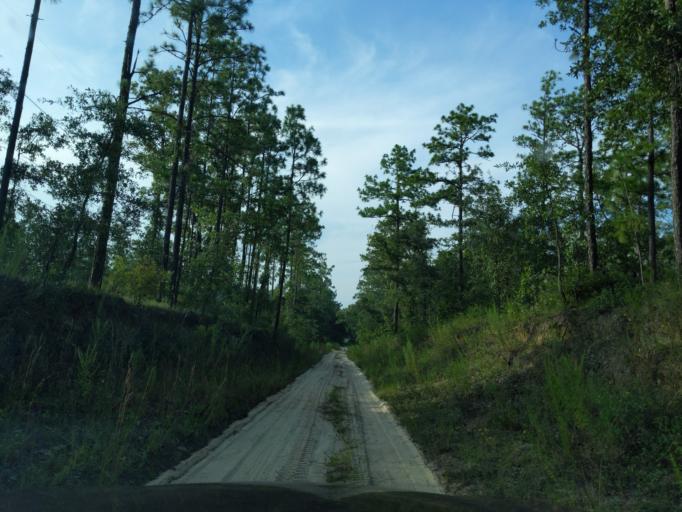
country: US
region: Florida
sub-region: Leon County
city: Tallahassee
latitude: 30.3632
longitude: -84.3611
